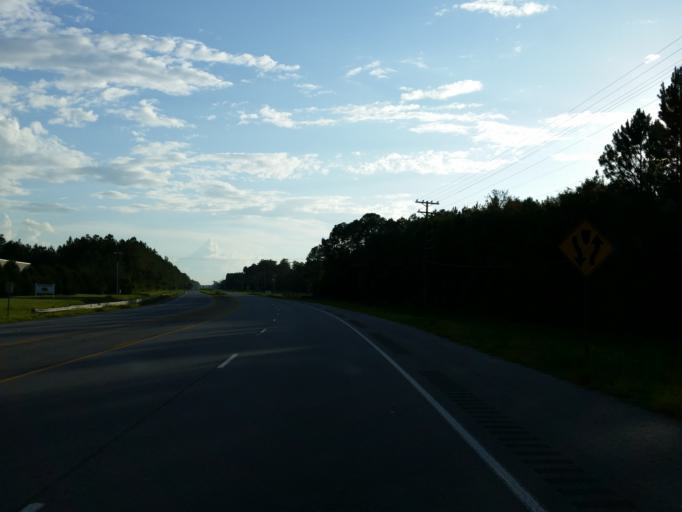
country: US
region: Georgia
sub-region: Clinch County
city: Homerville
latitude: 31.0302
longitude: -82.7790
